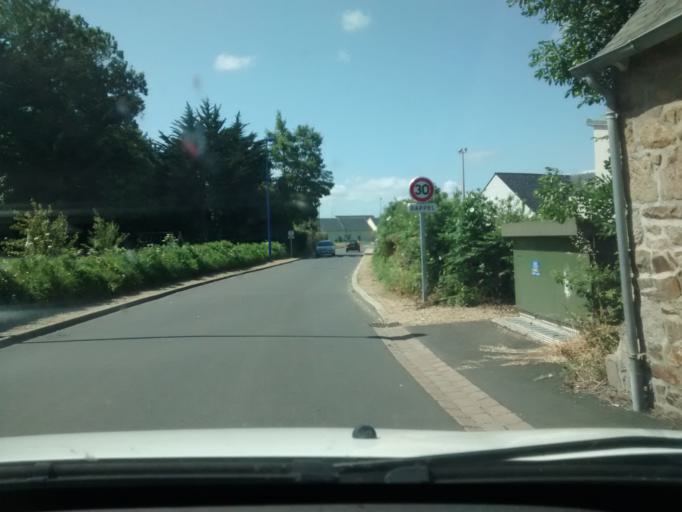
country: FR
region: Brittany
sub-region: Departement des Cotes-d'Armor
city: Louannec
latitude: 48.7957
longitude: -3.4075
